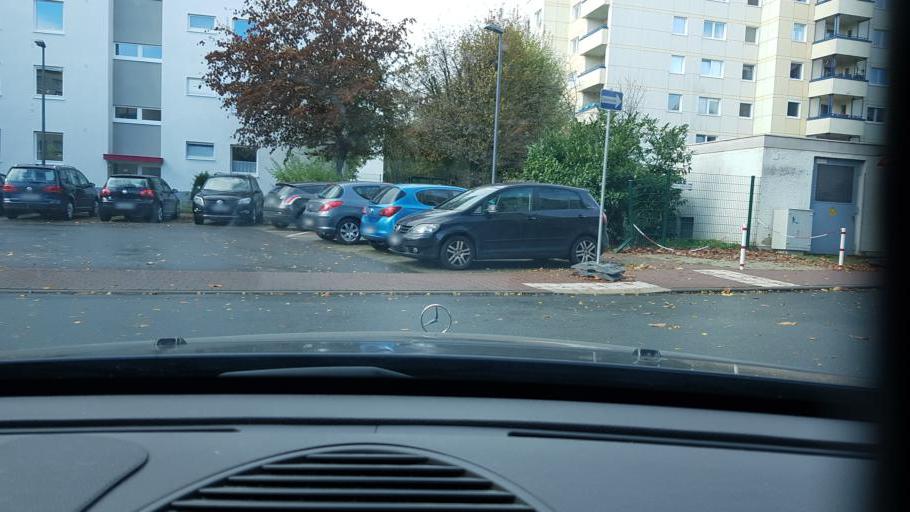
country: DE
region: Hesse
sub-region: Regierungsbezirk Darmstadt
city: Steinbach am Taunus
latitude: 50.1652
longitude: 8.5841
